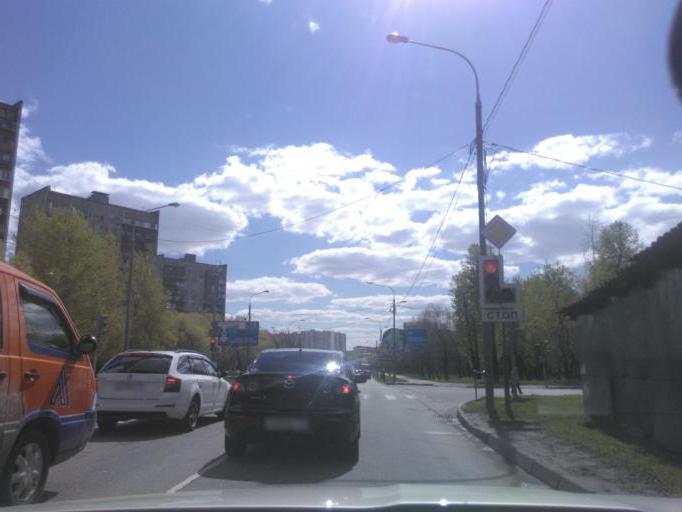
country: RU
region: Moscow
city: Novokhovrino
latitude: 55.8581
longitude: 37.5110
